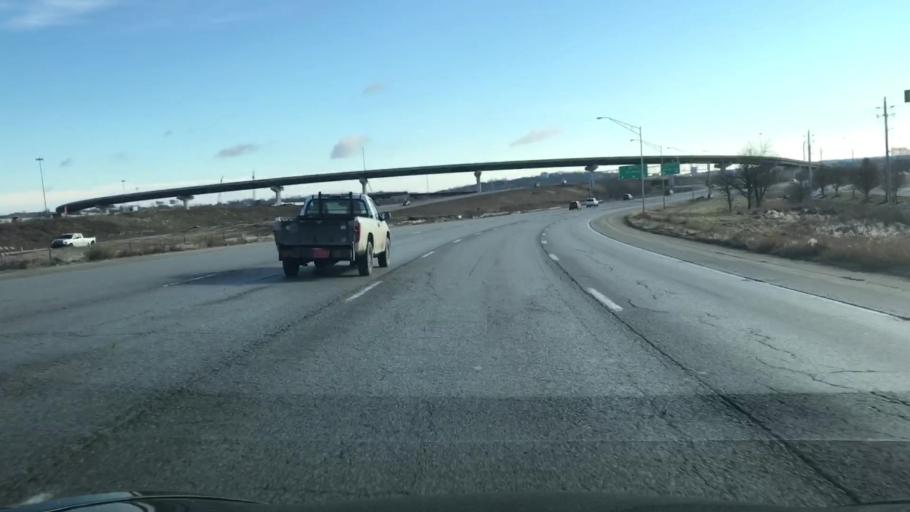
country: US
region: Iowa
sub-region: Pottawattamie County
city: Council Bluffs
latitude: 41.2317
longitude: -95.8460
